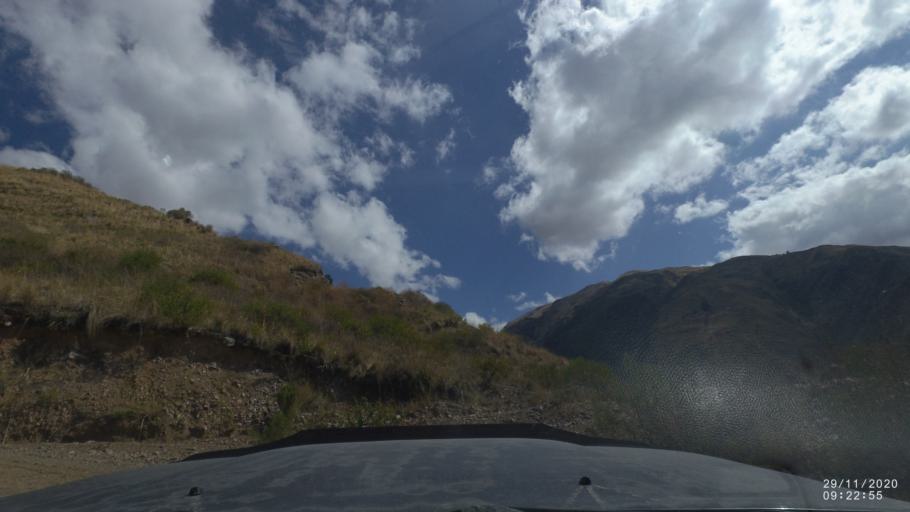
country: BO
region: Cochabamba
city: Cochabamba
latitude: -17.3221
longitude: -66.1863
